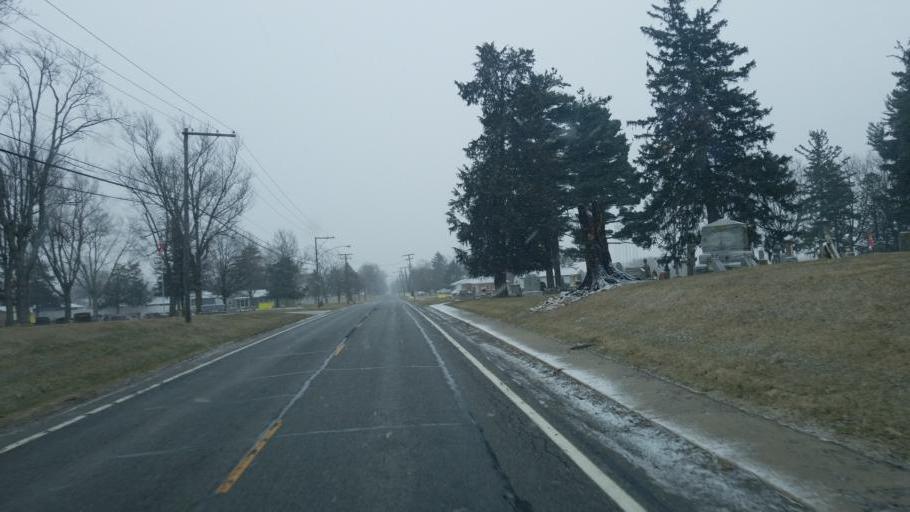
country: US
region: Ohio
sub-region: Defiance County
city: Hicksville
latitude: 41.3029
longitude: -84.7763
